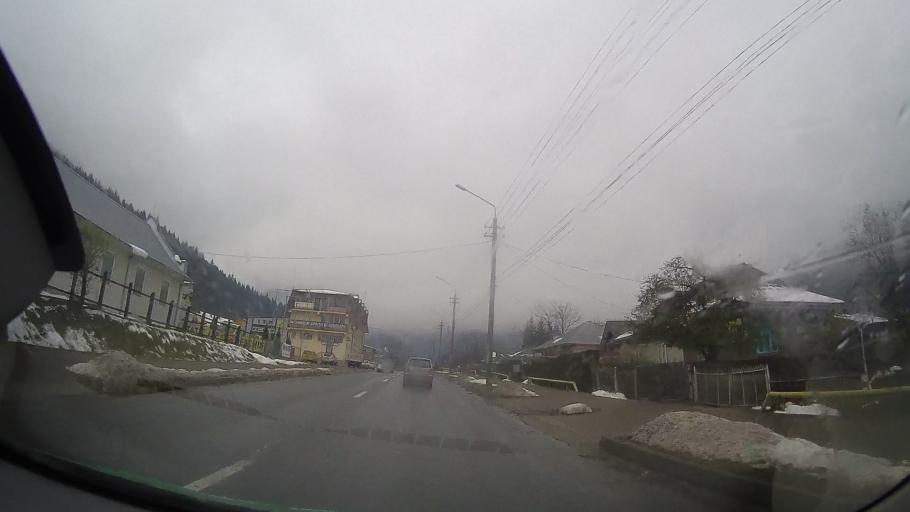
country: RO
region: Neamt
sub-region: Comuna Bicaz
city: Dodeni
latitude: 46.9087
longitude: 26.1012
